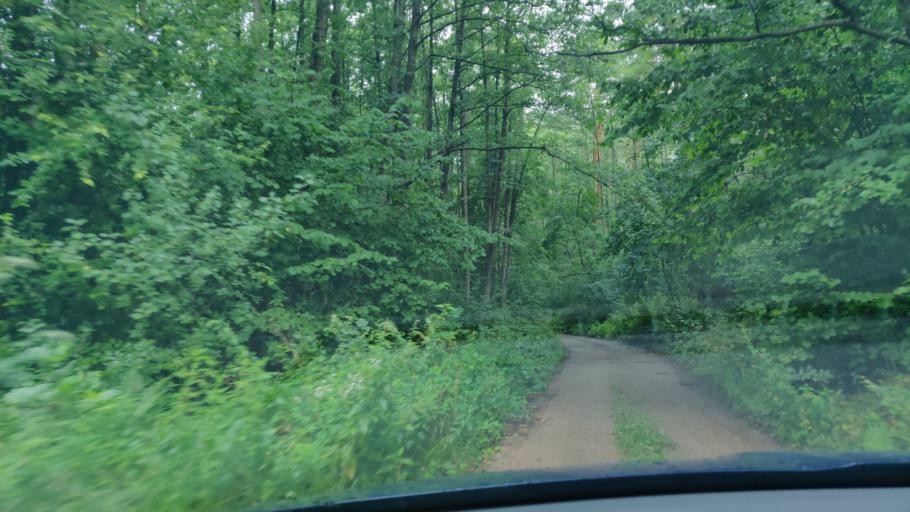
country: LT
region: Vilnius County
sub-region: Trakai
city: Rudiskes
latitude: 54.6067
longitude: 24.8430
